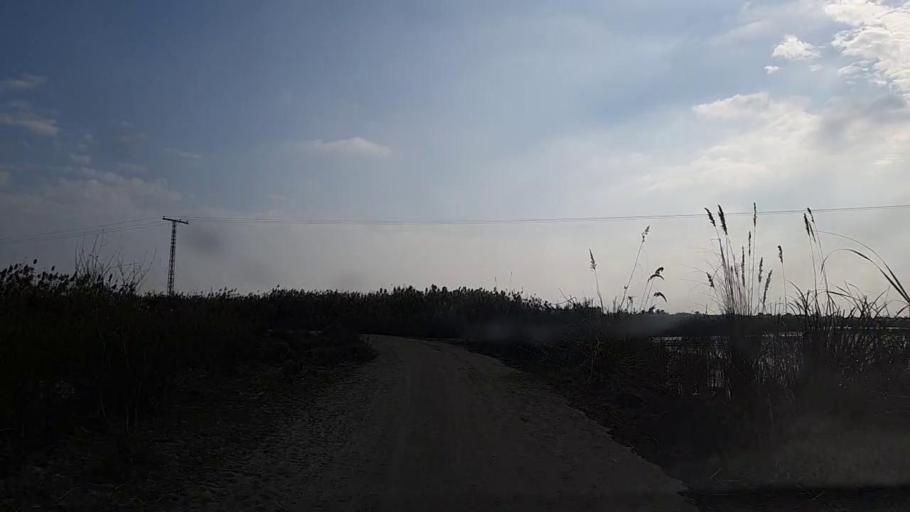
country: PK
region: Sindh
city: Sanghar
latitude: 26.2056
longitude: 69.0214
